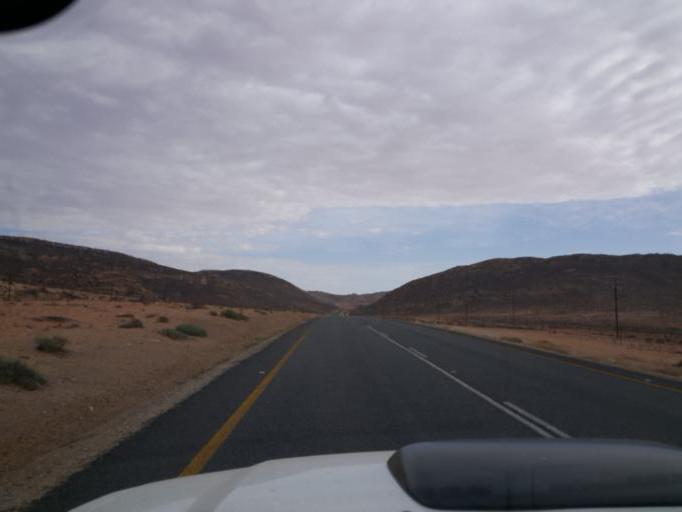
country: ZA
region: Northern Cape
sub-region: Namakwa District Municipality
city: Springbok
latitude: -29.4615
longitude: 17.8382
